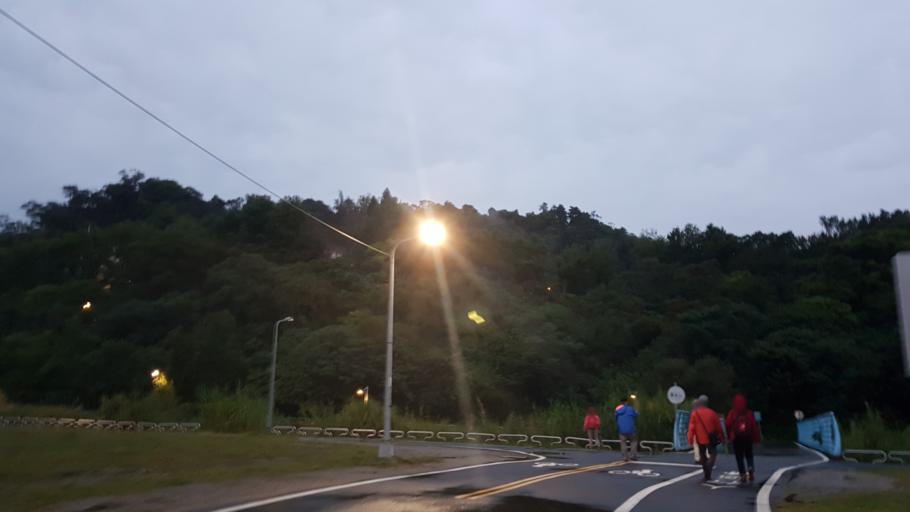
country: TW
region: Taipei
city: Taipei
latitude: 24.9831
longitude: 121.5720
